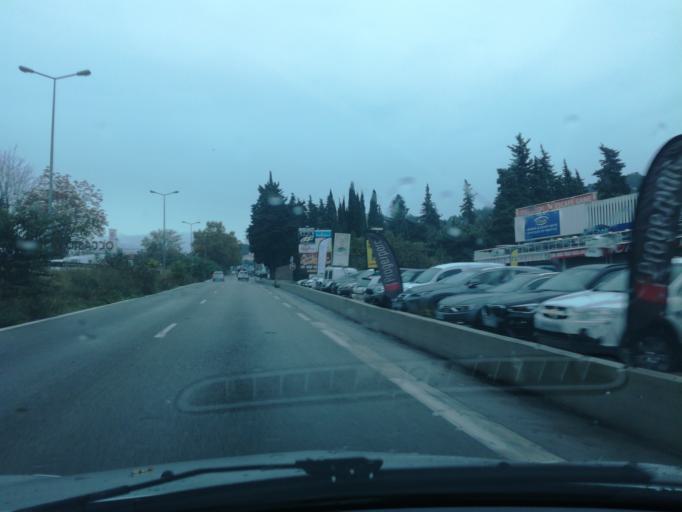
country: FR
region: Provence-Alpes-Cote d'Azur
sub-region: Departement des Alpes-Maritimes
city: Le Cannet
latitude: 43.5800
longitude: 7.0112
